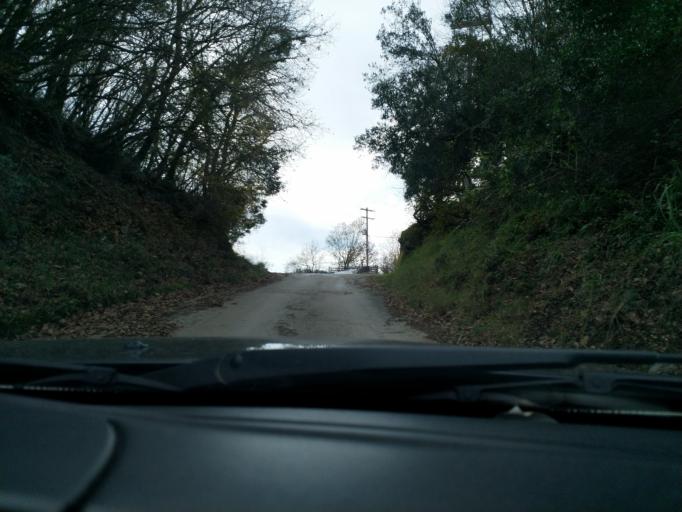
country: GR
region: Epirus
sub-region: Nomos Prevezis
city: Filippiada
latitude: 39.2347
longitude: 20.8452
